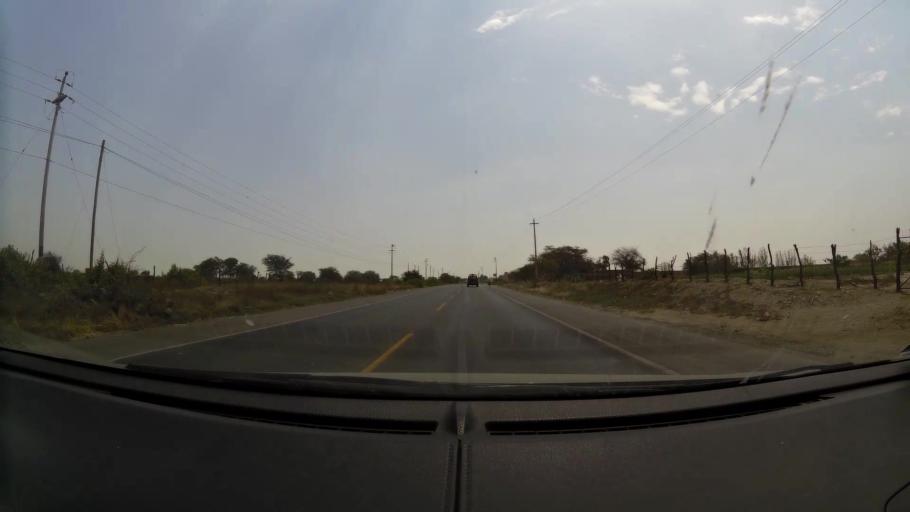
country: PE
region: La Libertad
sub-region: Chepen
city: Pacanga
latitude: -7.1403
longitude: -79.4626
